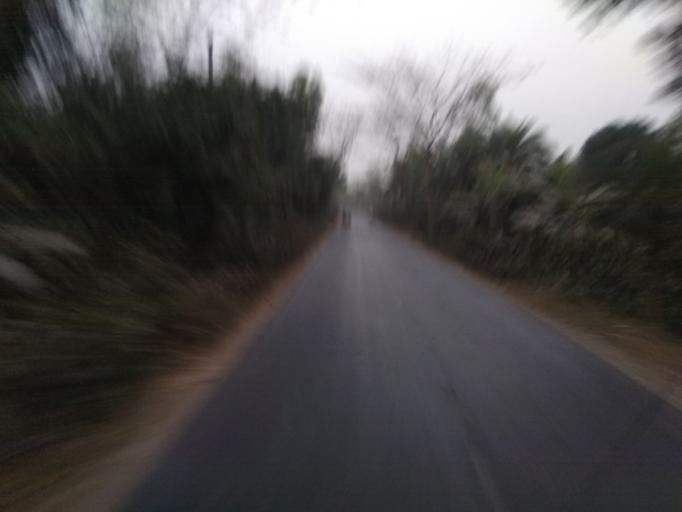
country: BD
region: Rajshahi
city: Bogra
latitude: 24.7315
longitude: 89.3241
